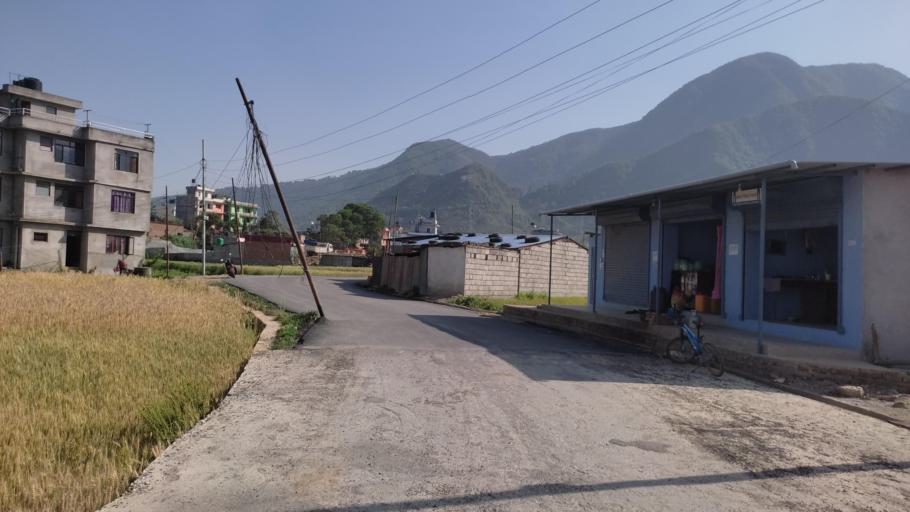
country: NP
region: Central Region
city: Kirtipur
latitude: 27.6680
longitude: 85.2711
